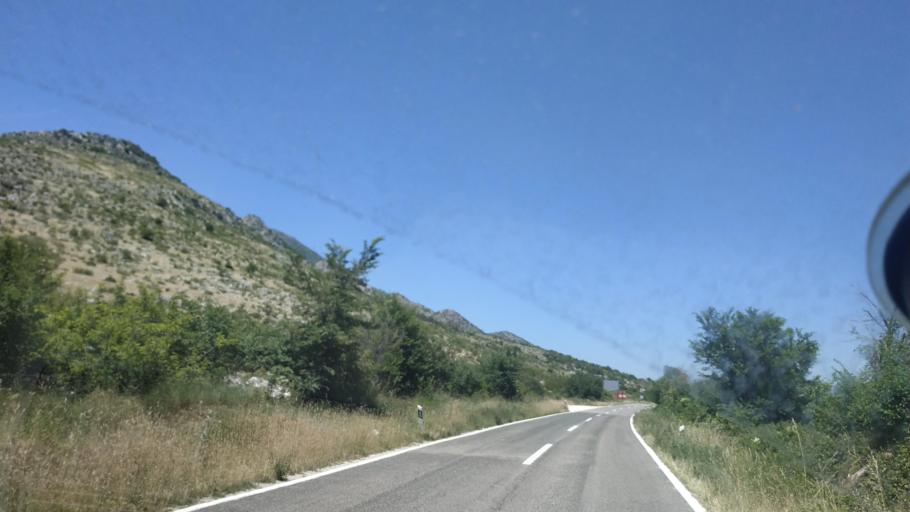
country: HR
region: Sibensko-Kniniska
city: Drnis
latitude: 43.9015
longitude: 16.2094
